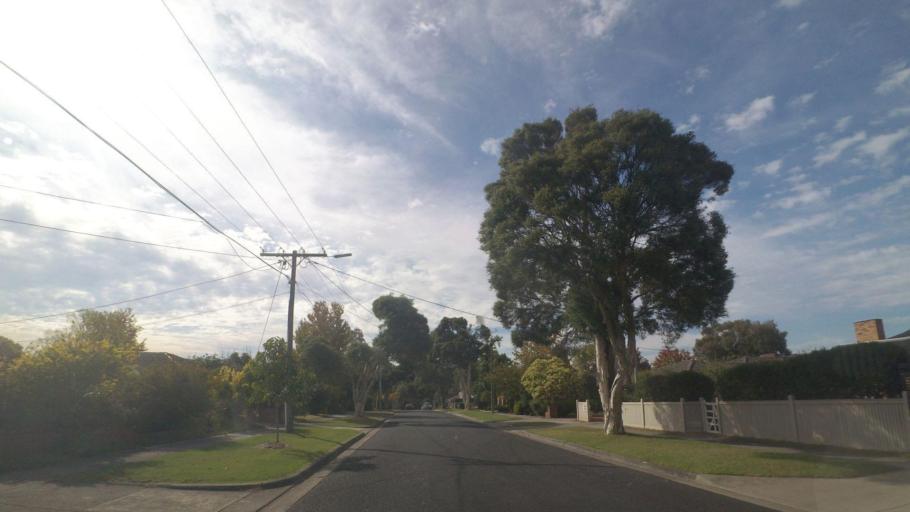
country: AU
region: Victoria
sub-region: Whitehorse
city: Blackburn
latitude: -37.8302
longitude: 145.1465
